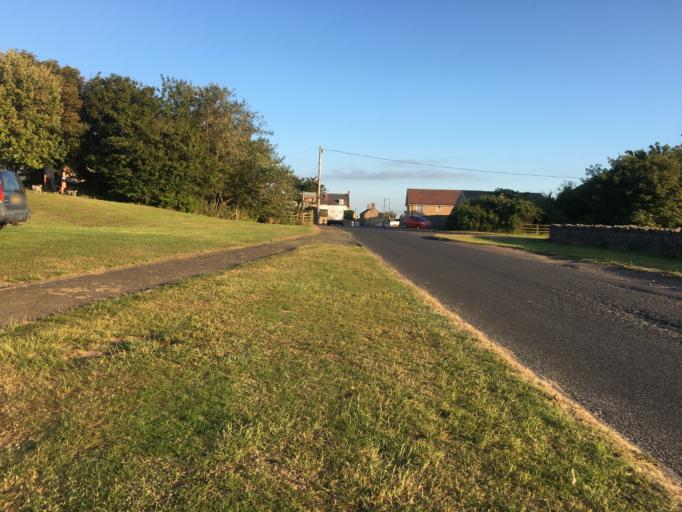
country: GB
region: England
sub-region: Northumberland
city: North Sunderland
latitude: 55.5783
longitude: -1.6680
